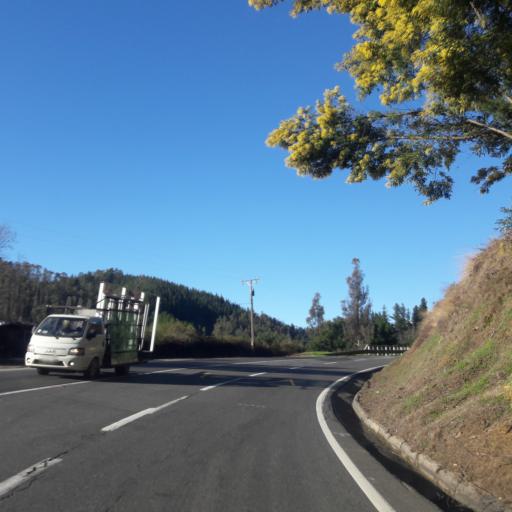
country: CL
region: Biobio
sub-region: Provincia de Biobio
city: La Laja
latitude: -37.2621
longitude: -72.9608
